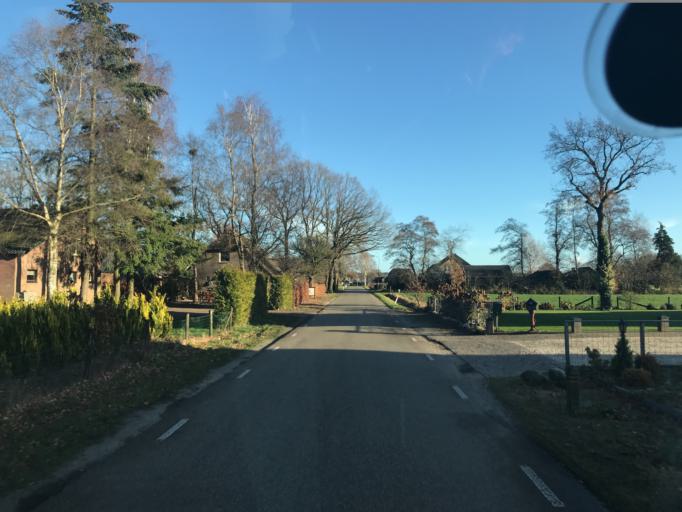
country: NL
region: Gelderland
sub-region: Gemeente Apeldoorn
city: Uddel
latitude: 52.2979
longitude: 5.7676
